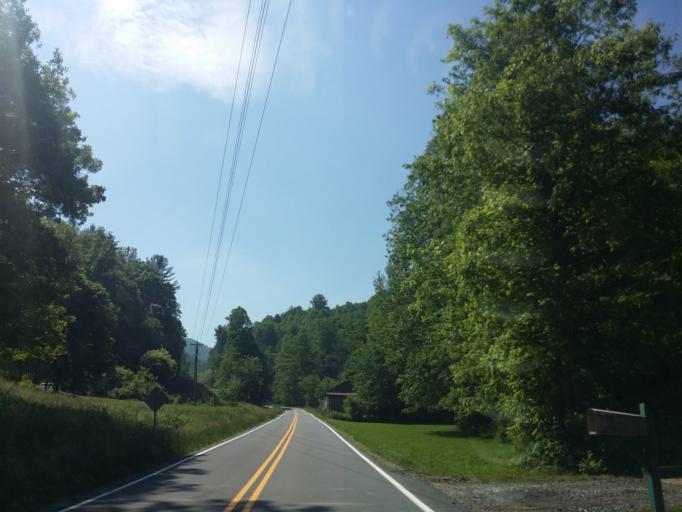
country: US
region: North Carolina
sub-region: Madison County
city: Marshall
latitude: 35.7477
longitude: -82.8614
